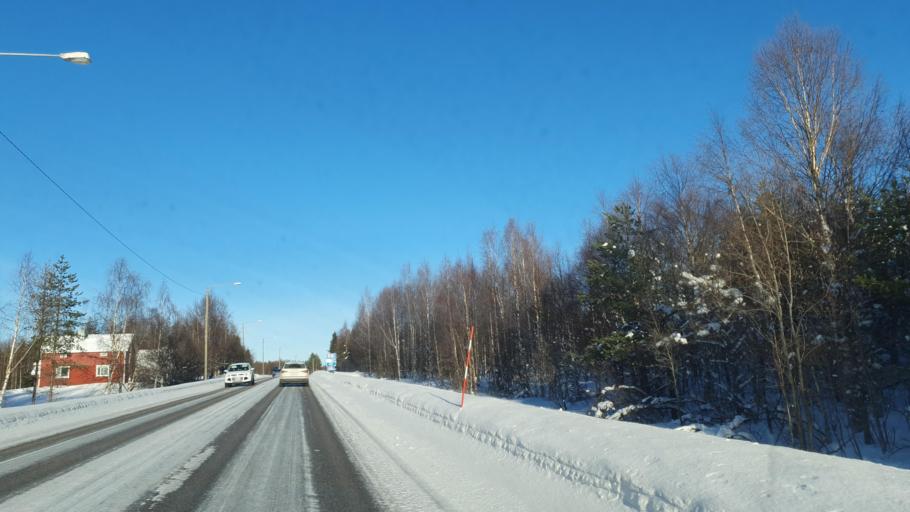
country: FI
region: Lapland
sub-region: Torniolaakso
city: Pello
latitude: 66.8842
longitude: 24.0727
